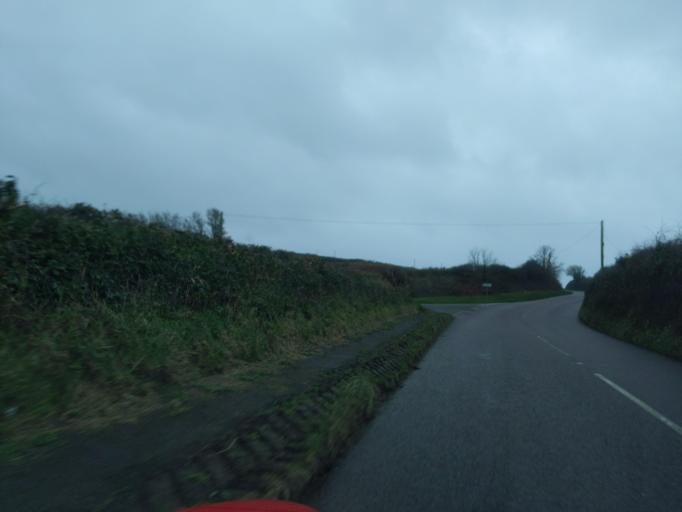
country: GB
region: England
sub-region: Cornwall
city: Saltash
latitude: 50.3622
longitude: -4.2660
